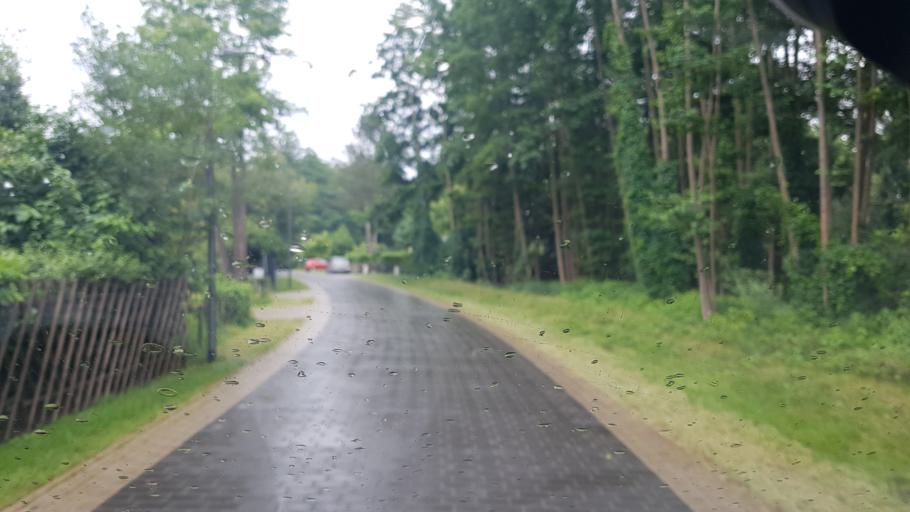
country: DE
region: Brandenburg
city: Teupitz
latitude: 52.1385
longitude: 13.6172
